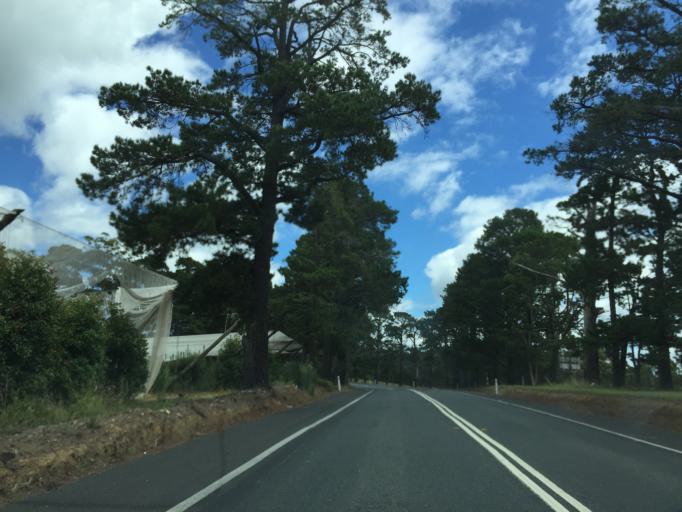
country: AU
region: New South Wales
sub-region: Hawkesbury
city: Richmond
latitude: -33.5082
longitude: 150.5564
